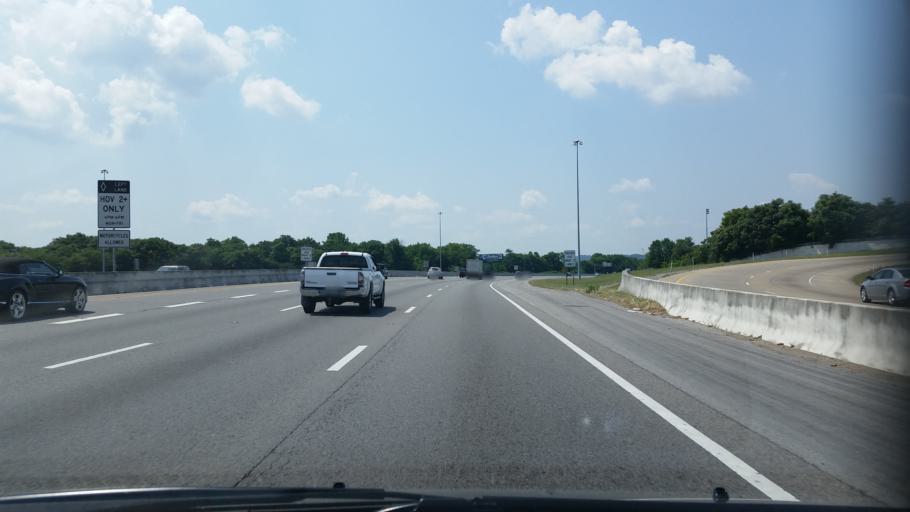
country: US
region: Tennessee
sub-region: Davidson County
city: Oak Hill
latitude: 36.0824
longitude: -86.7640
